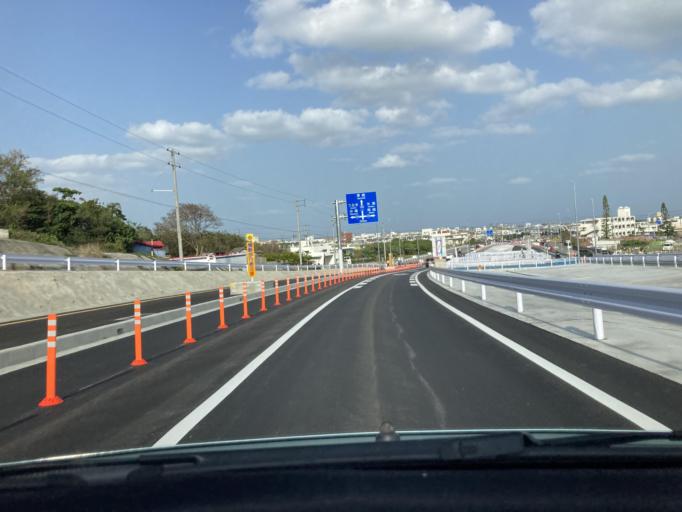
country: JP
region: Okinawa
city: Ginowan
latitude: 26.2114
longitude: 127.7564
